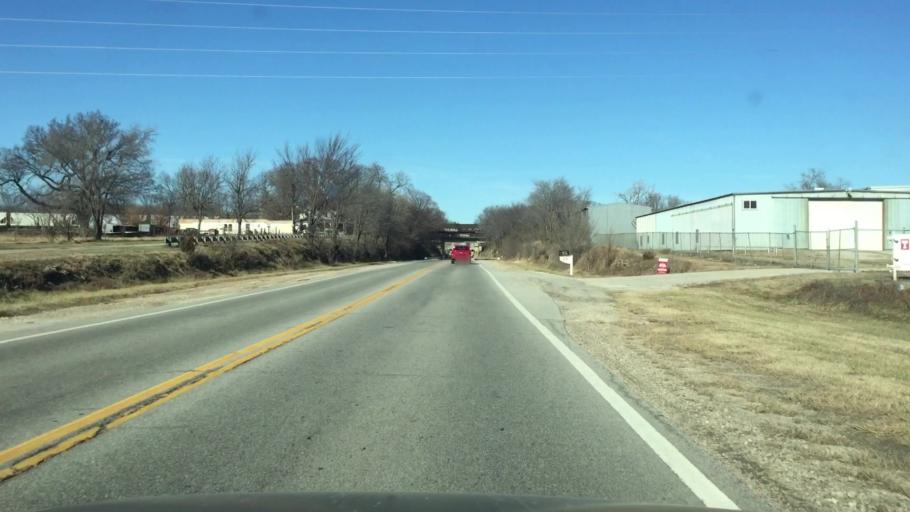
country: US
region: Kansas
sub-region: Anderson County
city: Garnett
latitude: 38.2715
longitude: -95.2492
